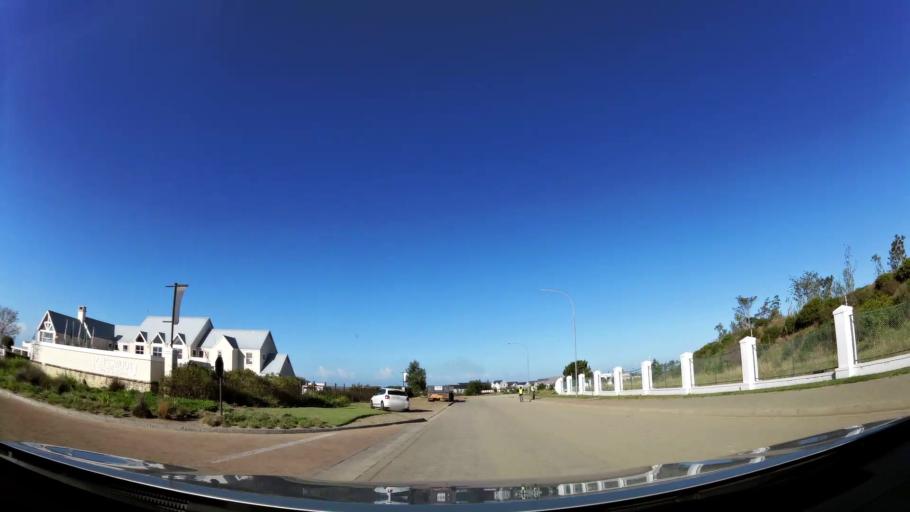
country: ZA
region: Western Cape
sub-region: Eden District Municipality
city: George
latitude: -33.9680
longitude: 22.4289
